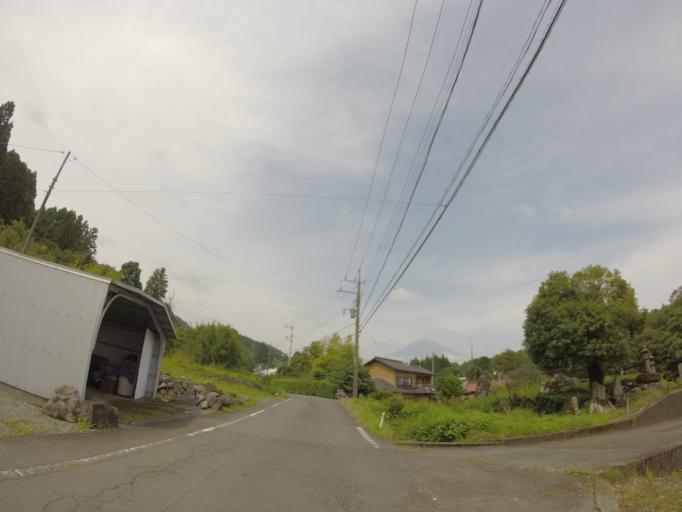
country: JP
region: Shizuoka
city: Fujinomiya
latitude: 35.2773
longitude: 138.5642
